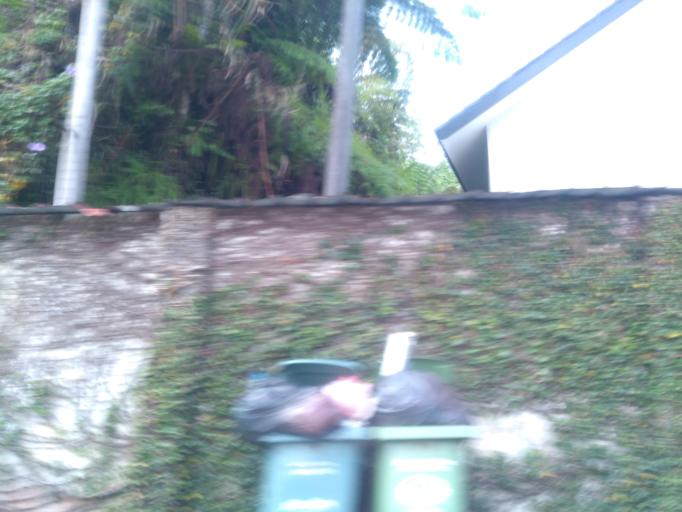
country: MY
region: Pahang
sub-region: Cameron Highlands
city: Tanah Rata
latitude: 4.4686
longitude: 101.3743
